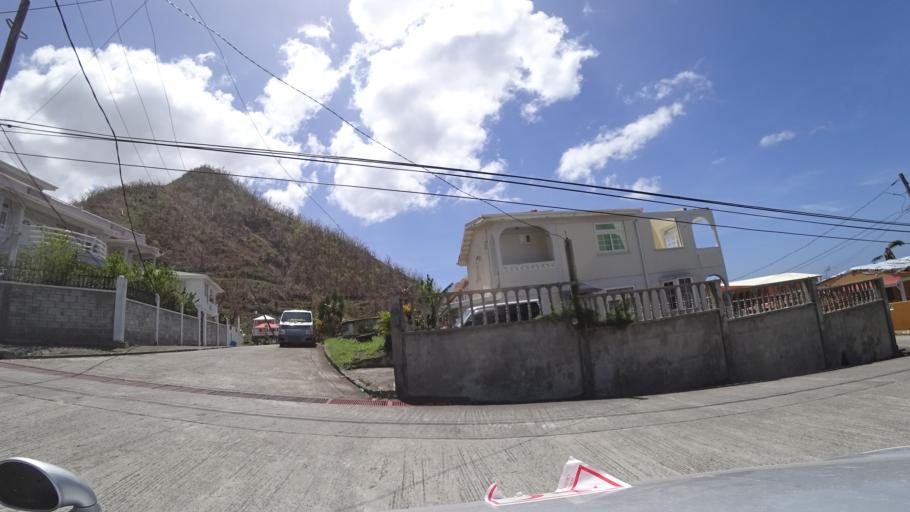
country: DM
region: Saint Luke
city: Pointe Michel
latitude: 15.2600
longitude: -61.3754
